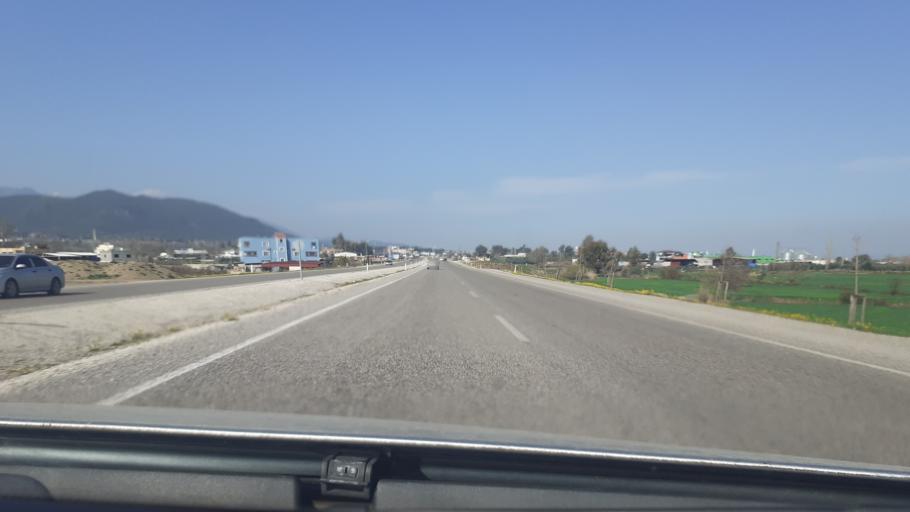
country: TR
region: Hatay
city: Aktepe
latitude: 36.6866
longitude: 36.4719
